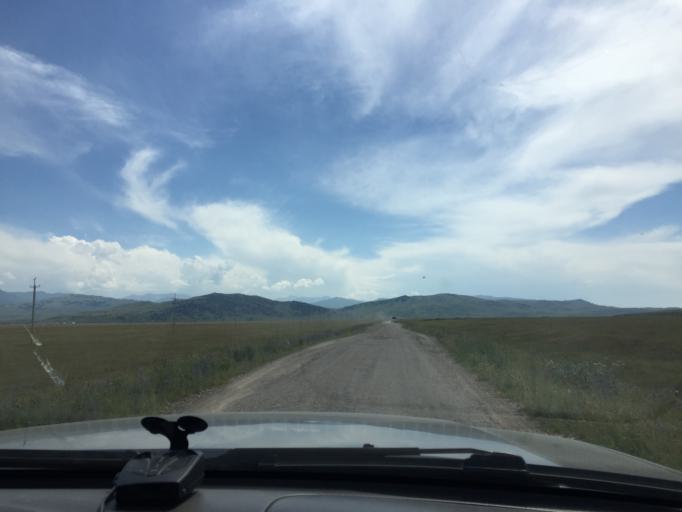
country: KZ
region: Almaty Oblysy
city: Kegen
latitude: 42.7986
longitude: 79.1785
